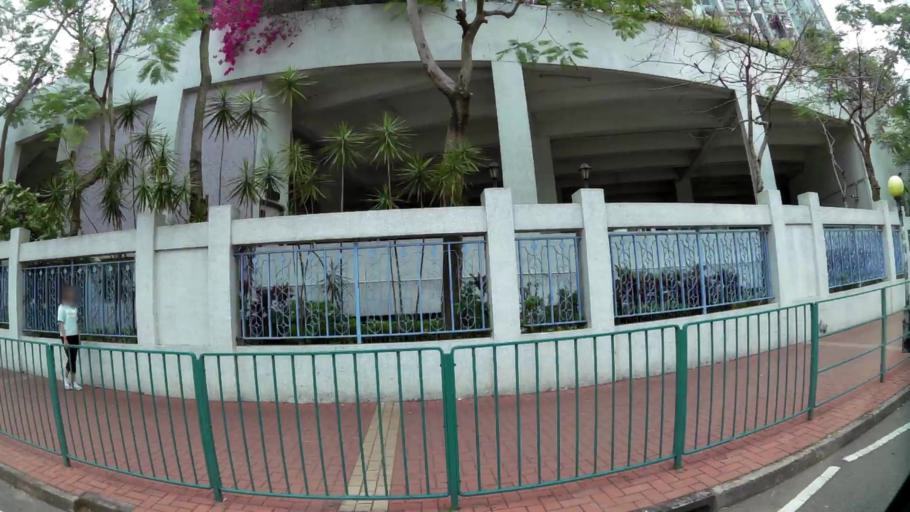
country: HK
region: Tuen Mun
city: Tuen Mun
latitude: 22.3727
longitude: 113.9692
